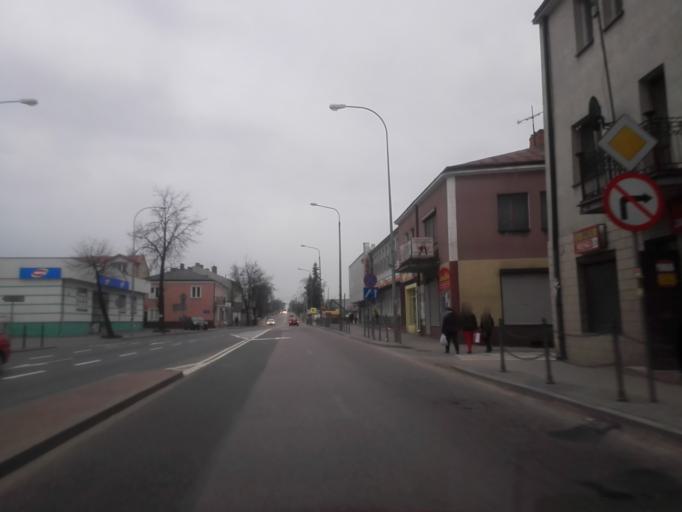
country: PL
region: Podlasie
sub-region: Powiat grajewski
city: Grajewo
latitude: 53.6467
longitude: 22.4542
